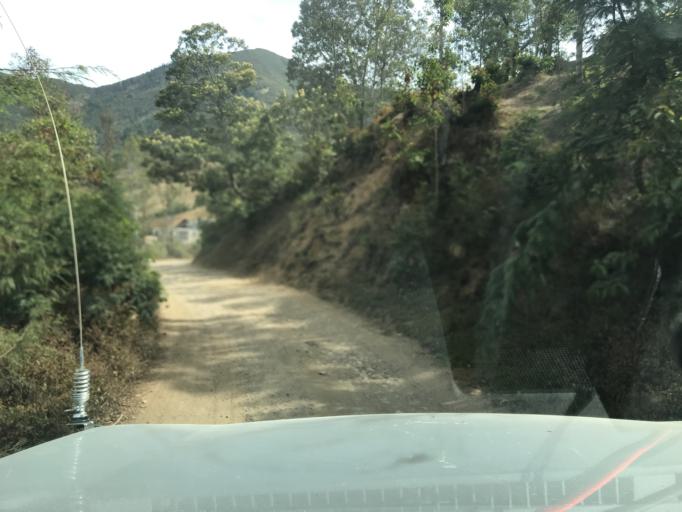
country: TL
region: Ainaro
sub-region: Ainaro
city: Ainaro
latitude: -8.8844
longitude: 125.5341
